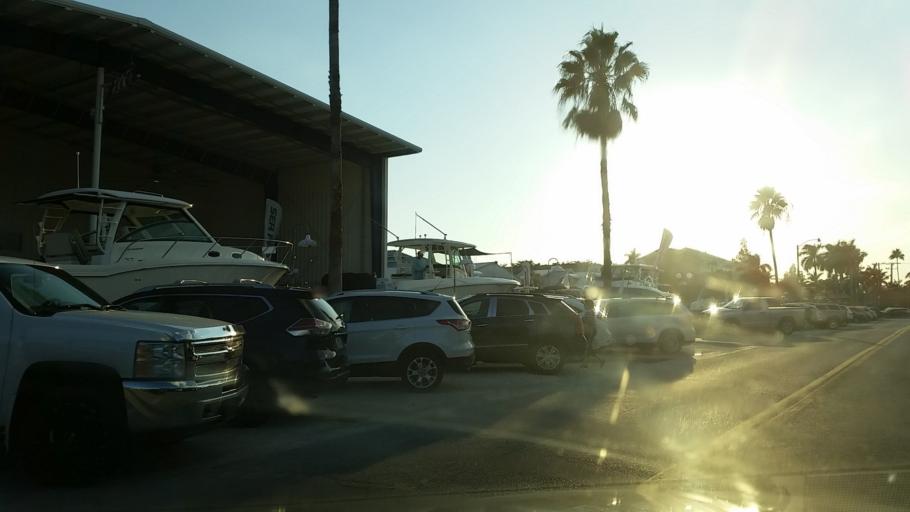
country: US
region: Florida
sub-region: Collier County
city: Naples
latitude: 26.1413
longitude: -81.7911
